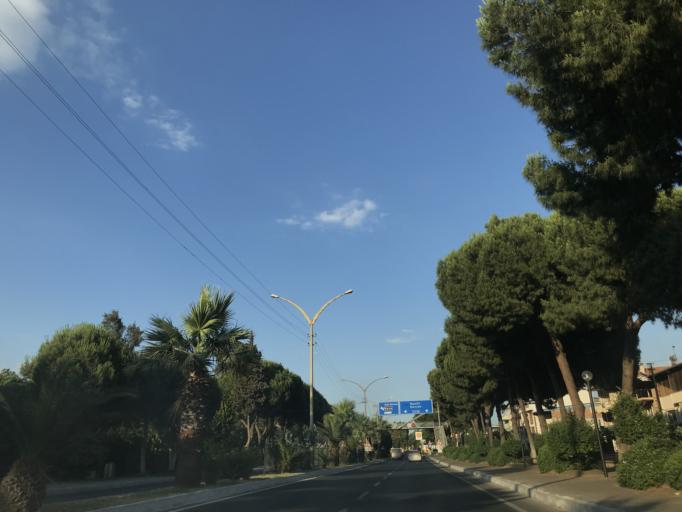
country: TR
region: Aydin
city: Sultanhisar
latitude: 37.8850
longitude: 28.1526
